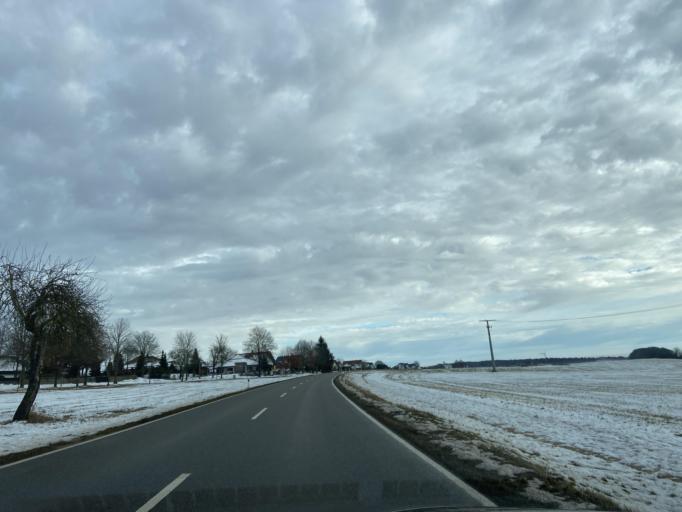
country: DE
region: Baden-Wuerttemberg
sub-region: Tuebingen Region
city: Hettingen
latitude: 48.1847
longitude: 9.2769
